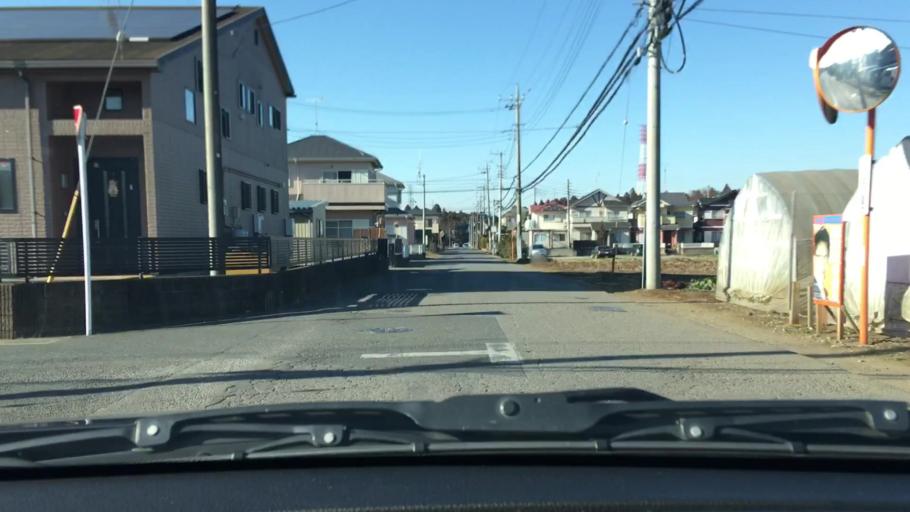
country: JP
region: Chiba
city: Shisui
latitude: 35.6969
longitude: 140.2926
